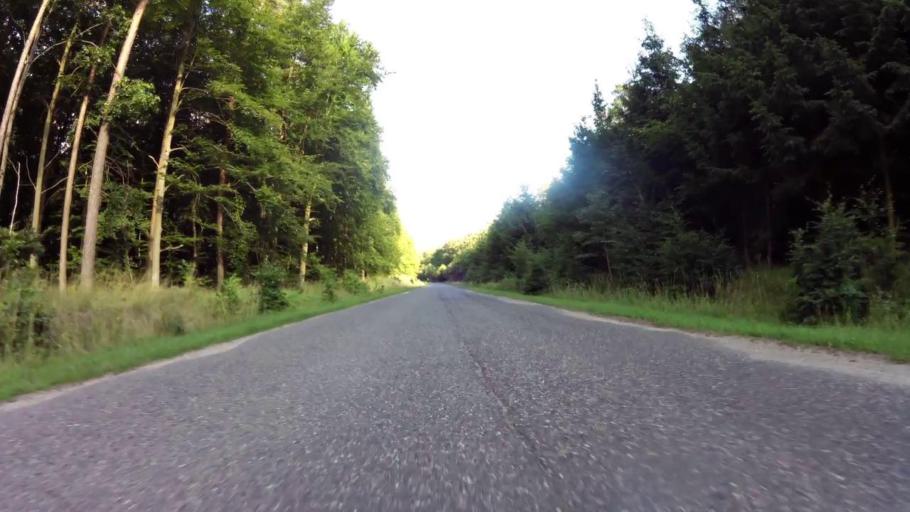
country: PL
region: West Pomeranian Voivodeship
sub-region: Powiat drawski
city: Drawsko Pomorskie
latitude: 53.4716
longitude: 15.8302
